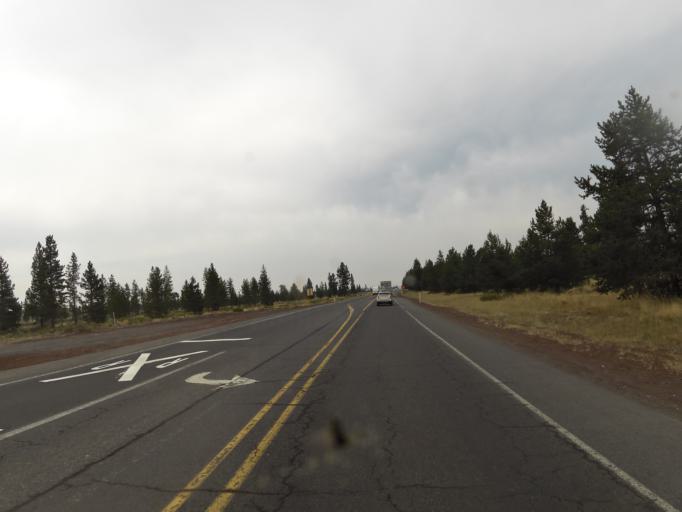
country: US
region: Oregon
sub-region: Deschutes County
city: La Pine
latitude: 43.7023
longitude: -121.4777
